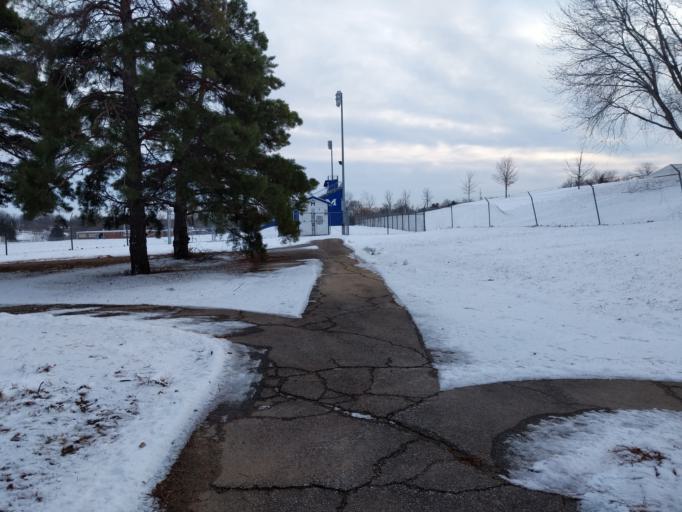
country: US
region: Kansas
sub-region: Riley County
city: Manhattan
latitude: 39.2013
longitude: -96.6201
